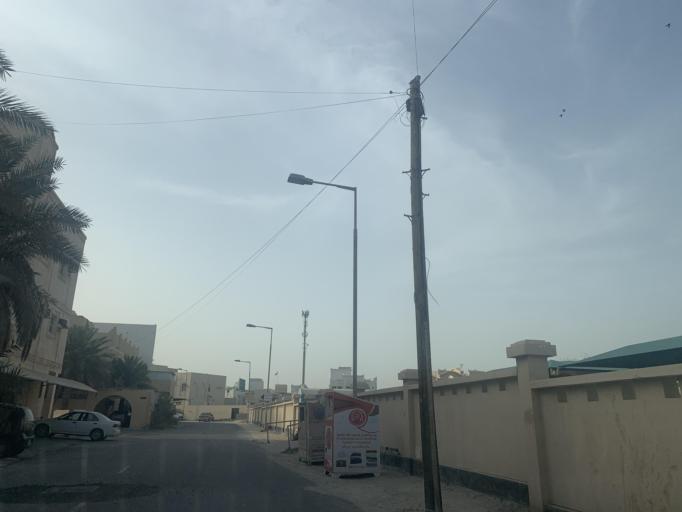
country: BH
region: Northern
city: Ar Rifa'
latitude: 26.1342
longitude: 50.5575
